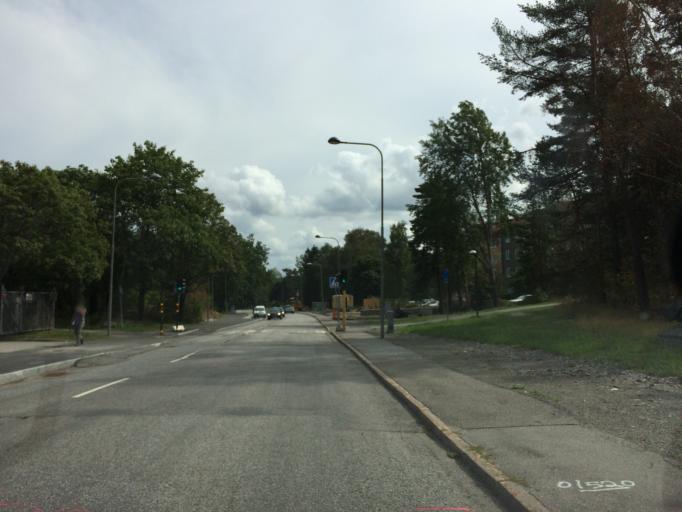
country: SE
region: Stockholm
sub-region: Stockholms Kommun
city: Arsta
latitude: 59.2889
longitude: 18.0038
